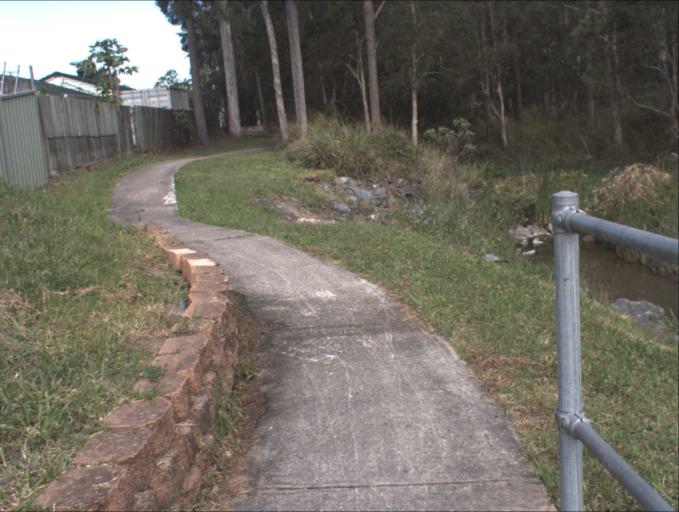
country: AU
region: Queensland
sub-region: Brisbane
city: Sunnybank Hills
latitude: -27.6616
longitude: 153.0316
